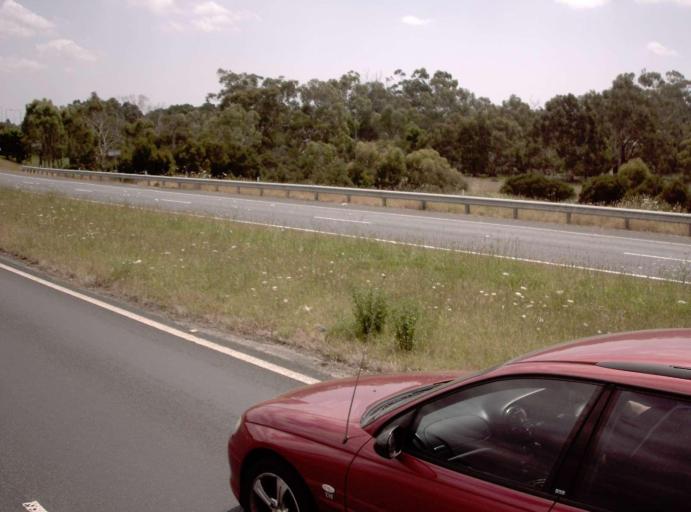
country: AU
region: Victoria
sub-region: Cardinia
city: Officer
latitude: -38.0589
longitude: 145.3758
